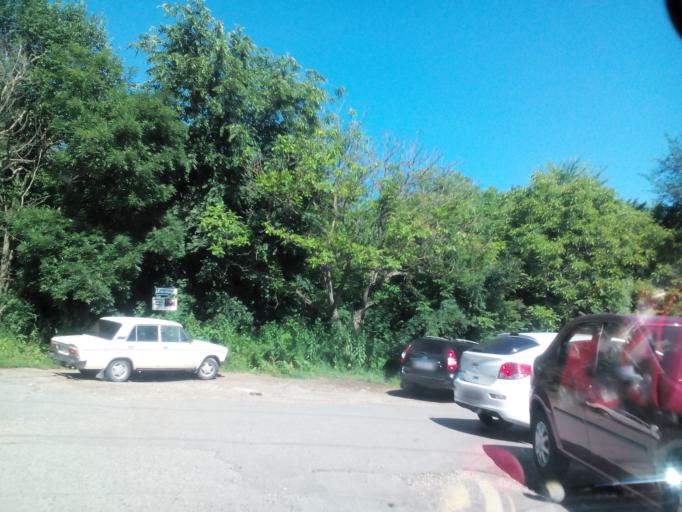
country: RU
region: Stavropol'skiy
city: Pyatigorsk
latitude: 44.0511
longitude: 43.0685
